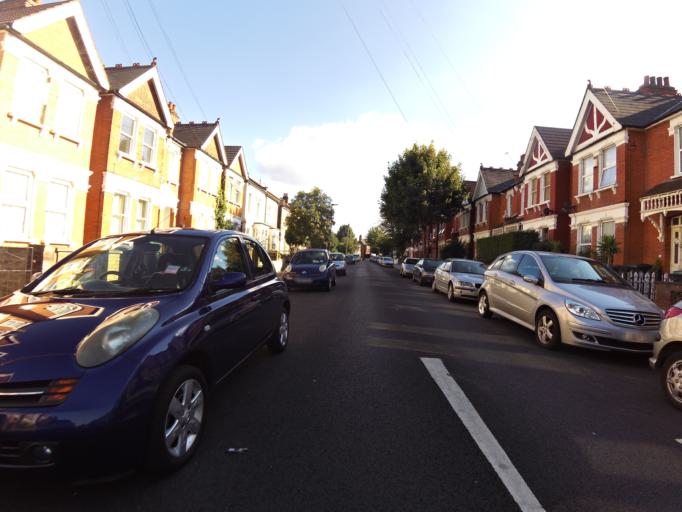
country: GB
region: England
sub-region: Greater London
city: Harringay
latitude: 51.5955
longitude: -0.0757
